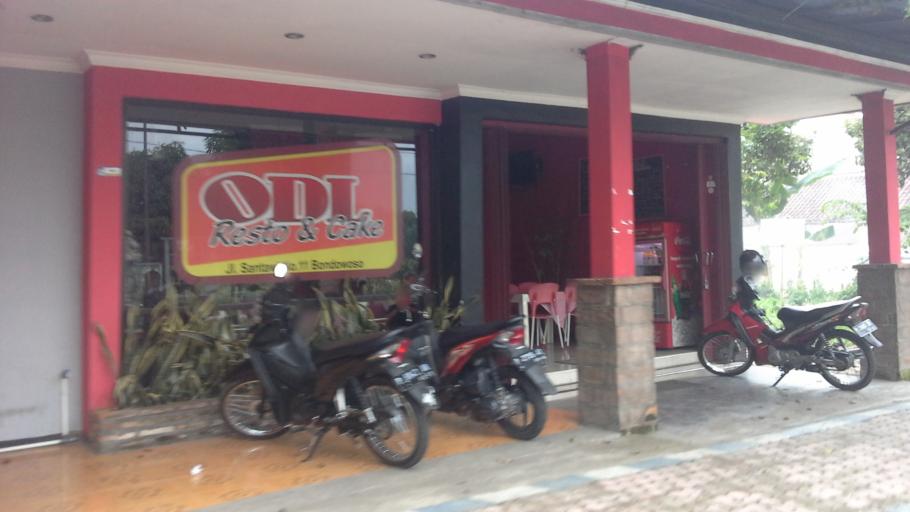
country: ID
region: East Java
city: Bondowoso
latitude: -7.9303
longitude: 113.8183
